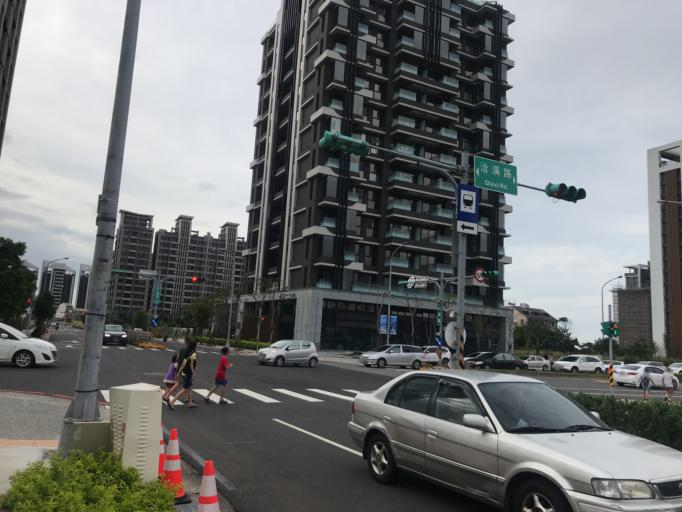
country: TW
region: Taiwan
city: Taoyuan City
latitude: 25.0073
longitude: 121.2062
